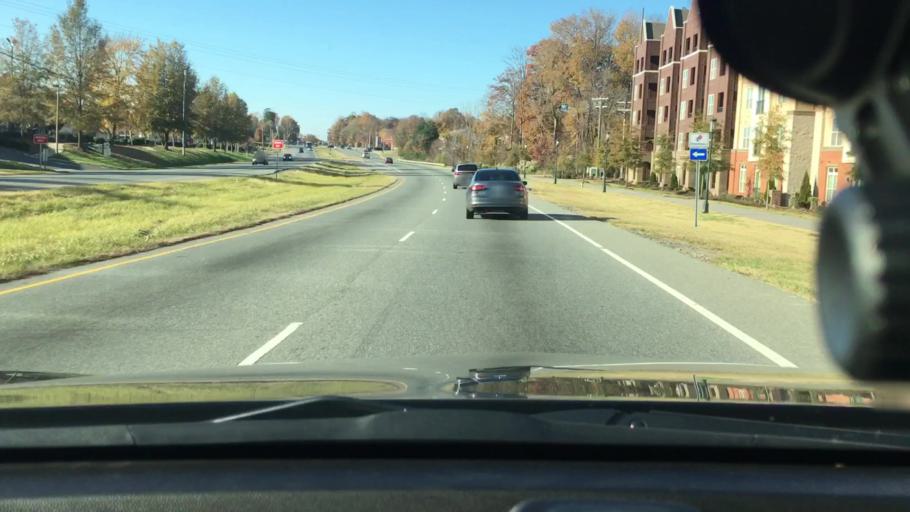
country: US
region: North Carolina
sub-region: Cabarrus County
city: Harrisburg
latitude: 35.3088
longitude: -80.7198
